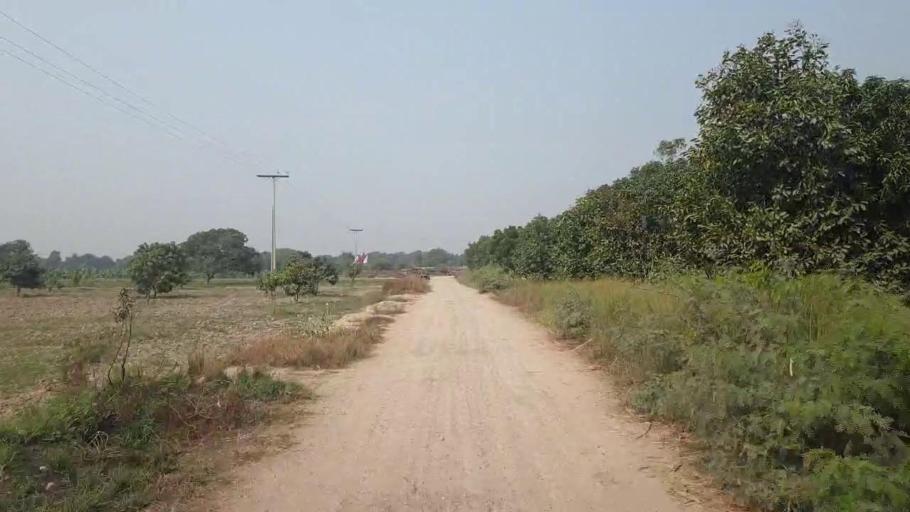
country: PK
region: Sindh
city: Tando Muhammad Khan
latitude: 25.2702
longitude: 68.5803
